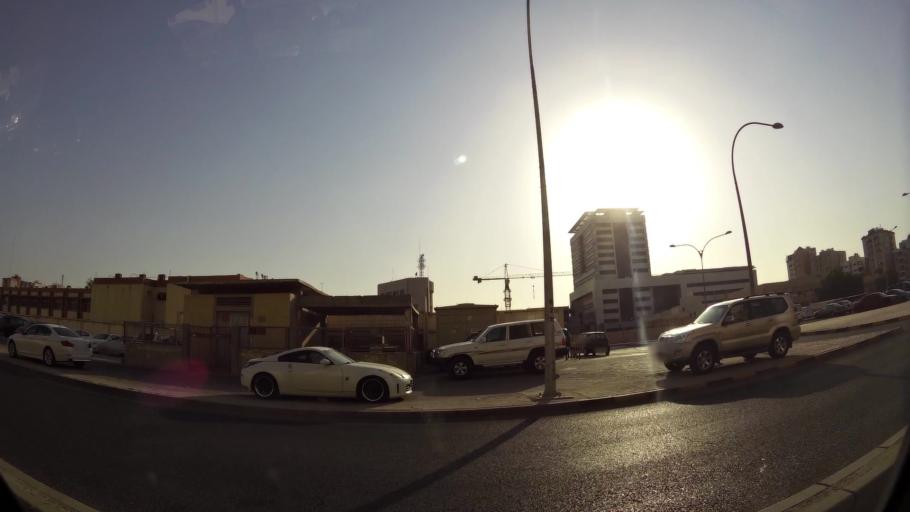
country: KW
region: Muhafazat Hawalli
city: As Salimiyah
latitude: 29.3321
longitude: 48.0842
